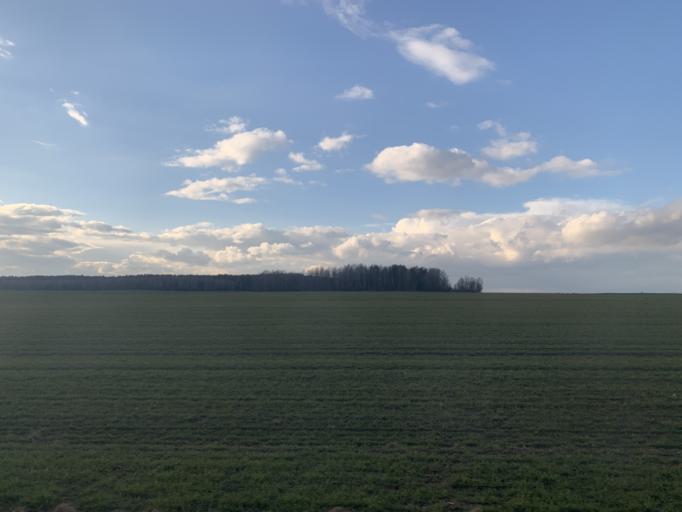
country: BY
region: Minsk
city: Novy Svyerzhan'
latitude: 53.3757
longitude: 26.7159
